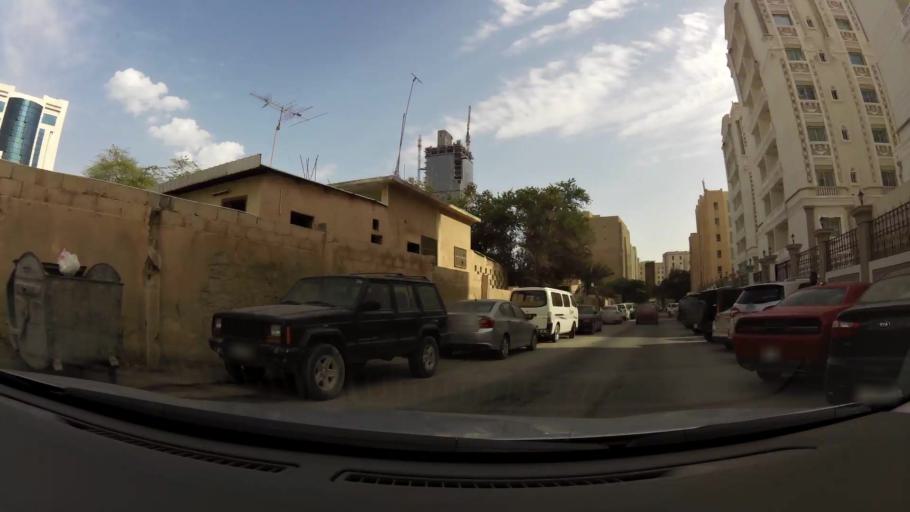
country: QA
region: Baladiyat ad Dawhah
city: Doha
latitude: 25.2886
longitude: 51.5151
